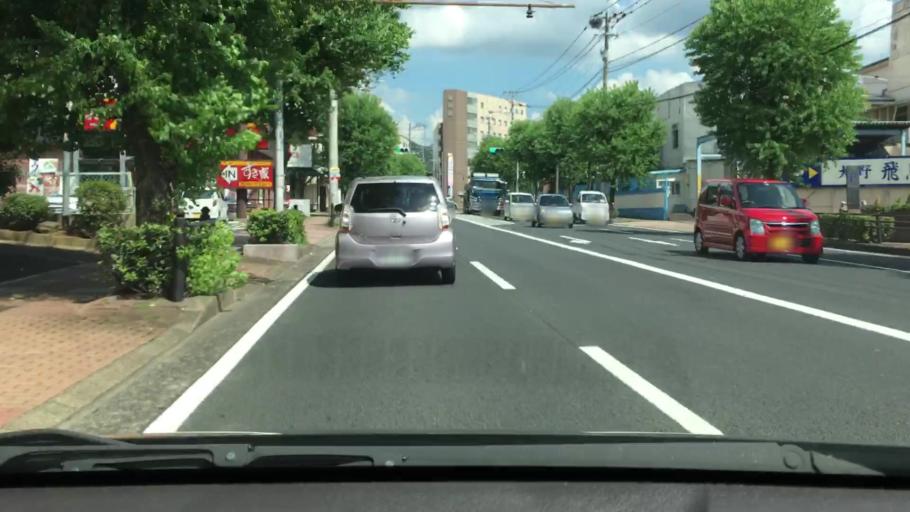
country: JP
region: Nagasaki
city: Sasebo
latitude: 33.2080
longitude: 129.7187
